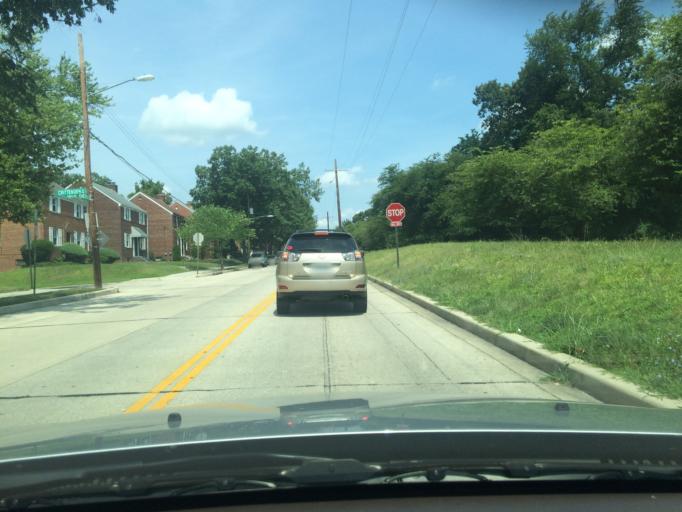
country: US
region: Maryland
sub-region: Prince George's County
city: Mount Rainier
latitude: 38.9474
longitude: -76.9796
